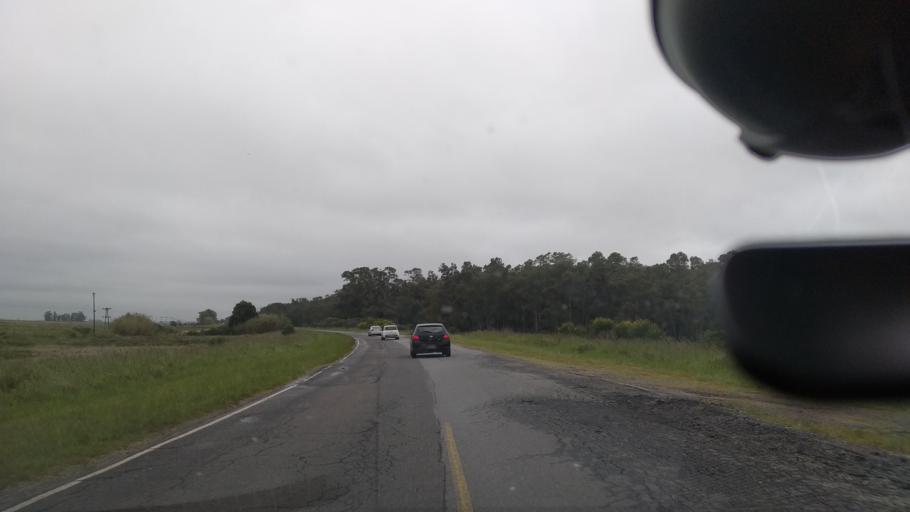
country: AR
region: Buenos Aires
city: Veronica
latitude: -35.4677
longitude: -57.3241
